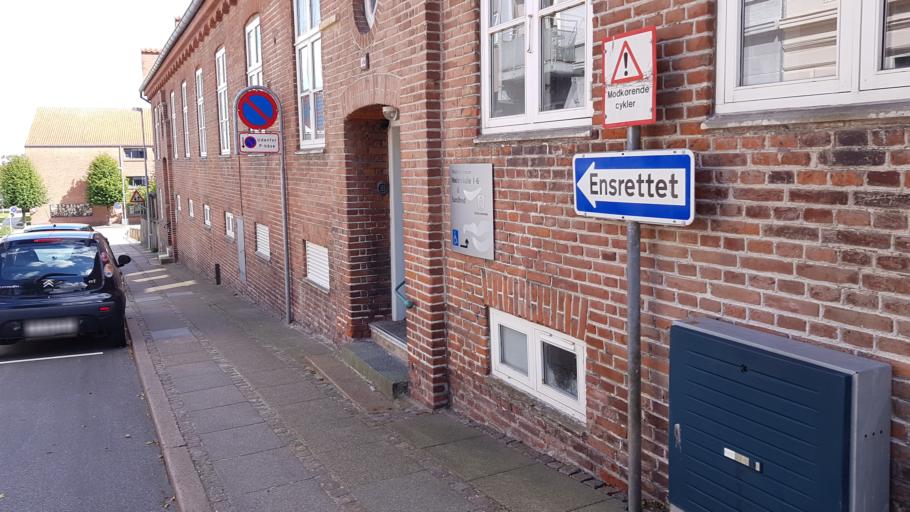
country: DK
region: North Denmark
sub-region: Thisted Kommune
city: Thisted
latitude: 56.9533
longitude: 8.6902
